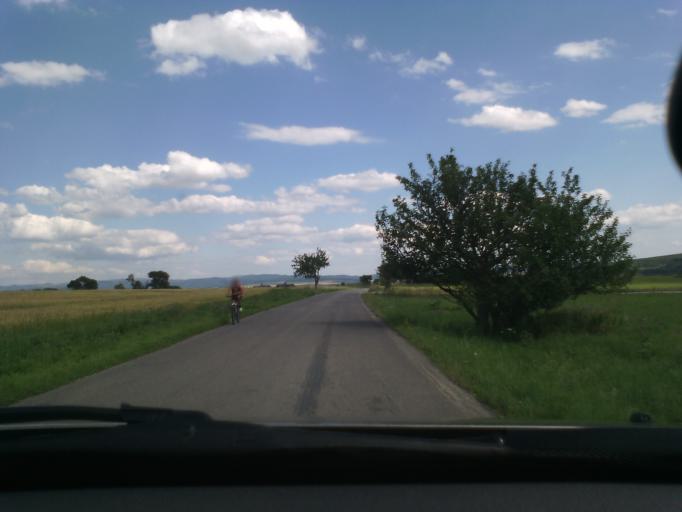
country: SK
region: Presovsky
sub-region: Okres Poprad
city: Nova Lesna
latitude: 49.1277
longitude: 20.3275
